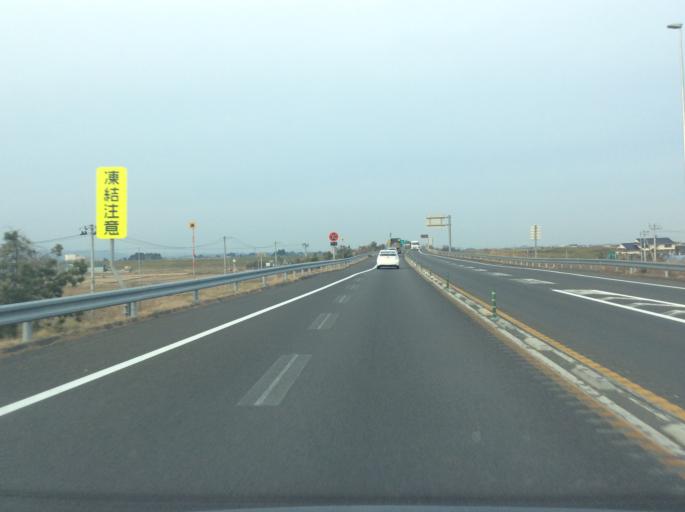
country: JP
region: Miyagi
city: Iwanuma
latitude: 38.0887
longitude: 140.8868
